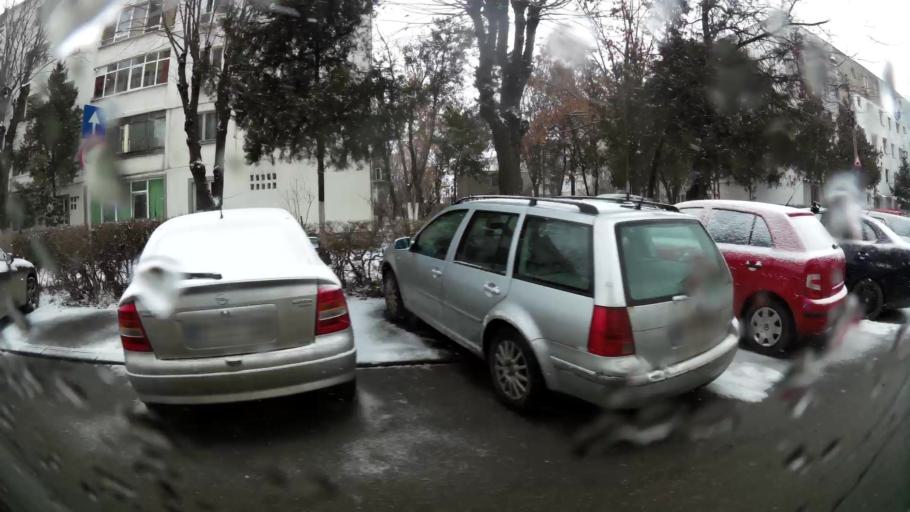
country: RO
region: Prahova
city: Ploiesti
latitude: 44.9361
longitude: 25.9828
